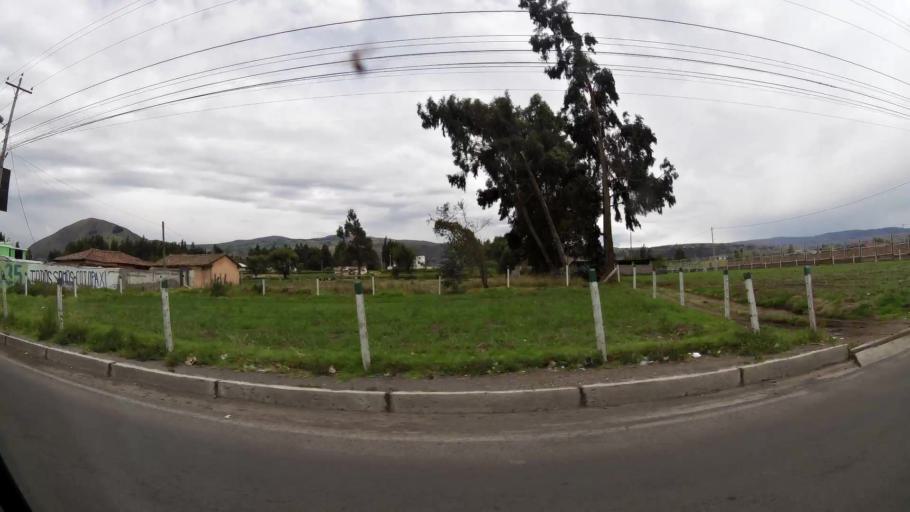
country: EC
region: Cotopaxi
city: San Miguel de Salcedo
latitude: -1.0156
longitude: -78.5924
